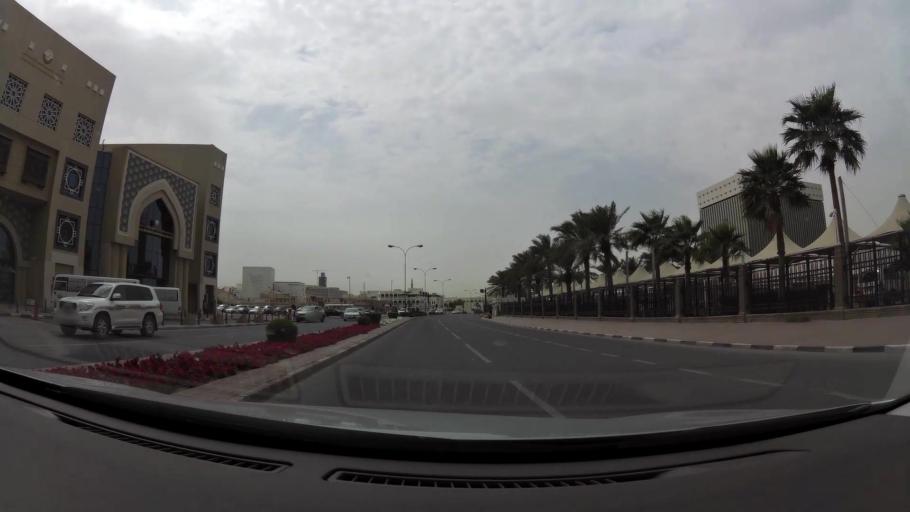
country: QA
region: Baladiyat ad Dawhah
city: Doha
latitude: 25.2896
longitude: 51.5361
